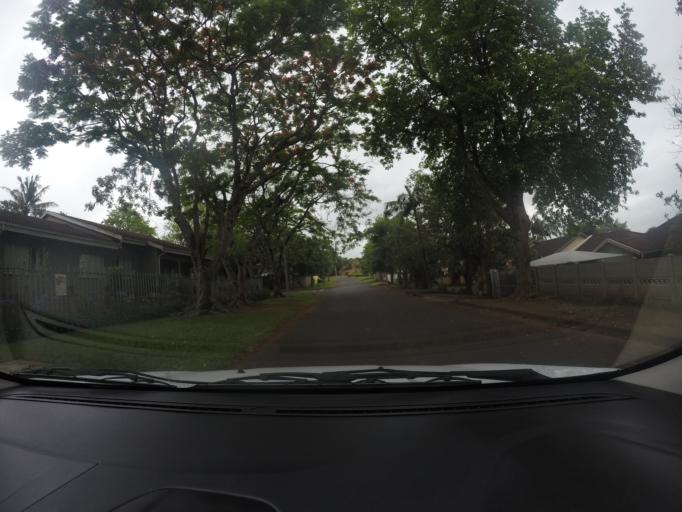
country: ZA
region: KwaZulu-Natal
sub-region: uThungulu District Municipality
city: Empangeni
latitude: -28.7659
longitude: 31.8914
